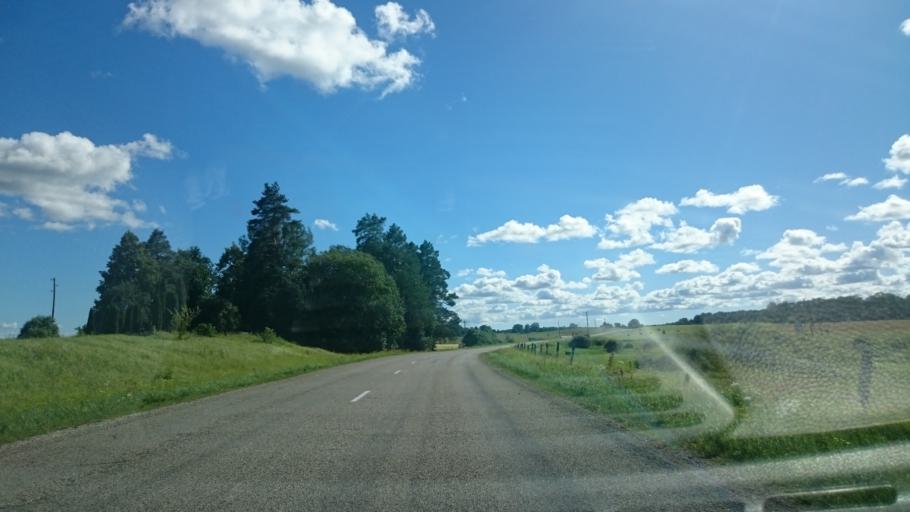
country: LV
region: Aizpute
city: Aizpute
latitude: 56.7762
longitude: 21.6342
